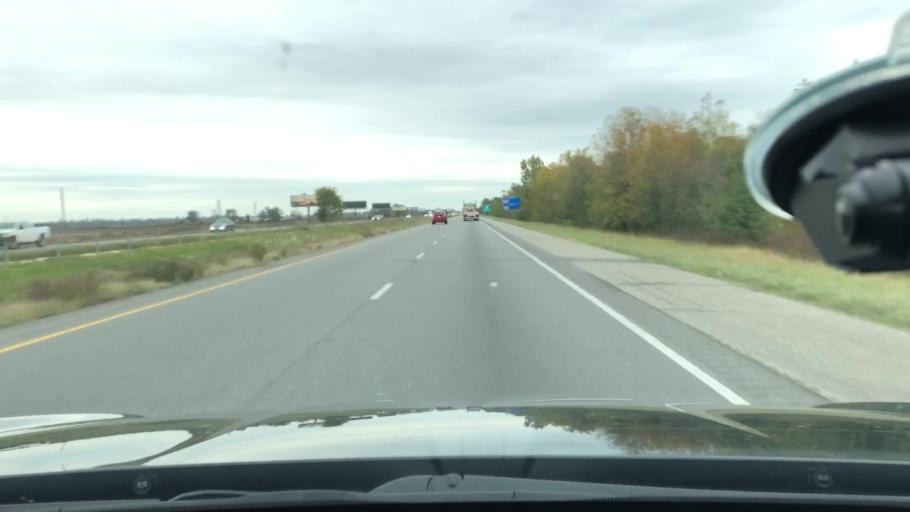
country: US
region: Arkansas
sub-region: Miller County
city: Texarkana
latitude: 33.4951
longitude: -93.9643
